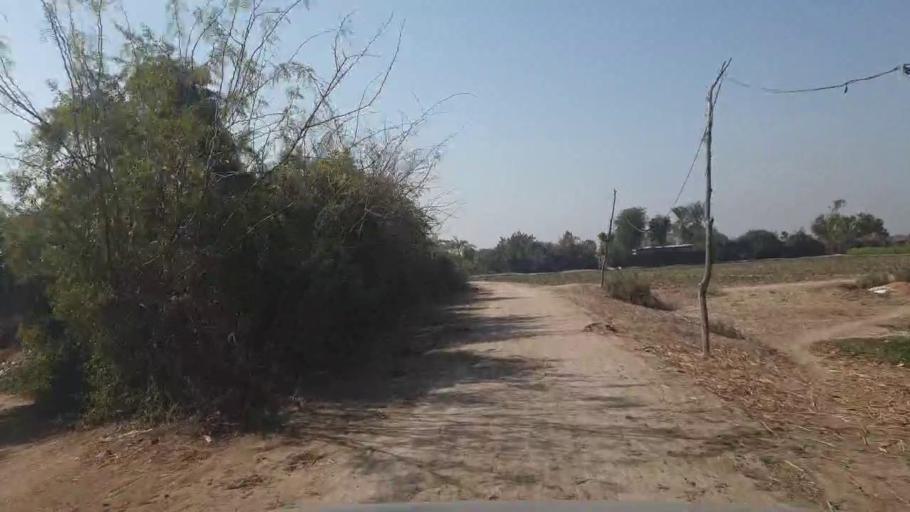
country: PK
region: Sindh
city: Chambar
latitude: 25.3608
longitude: 68.7795
